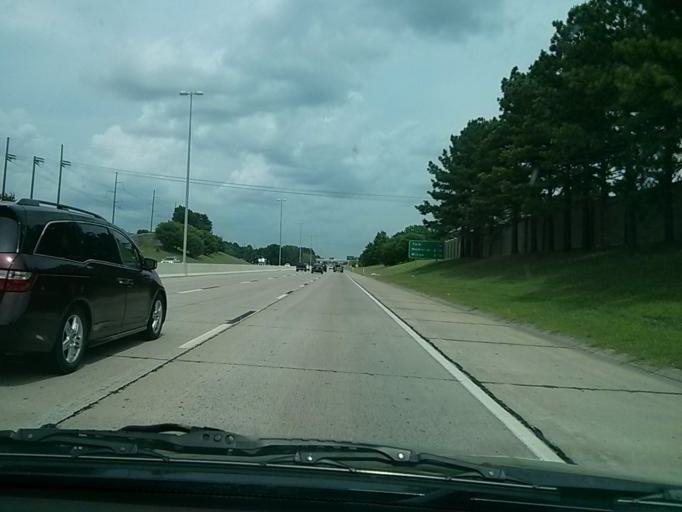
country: US
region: Oklahoma
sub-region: Tulsa County
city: Jenks
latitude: 36.0253
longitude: -95.9324
